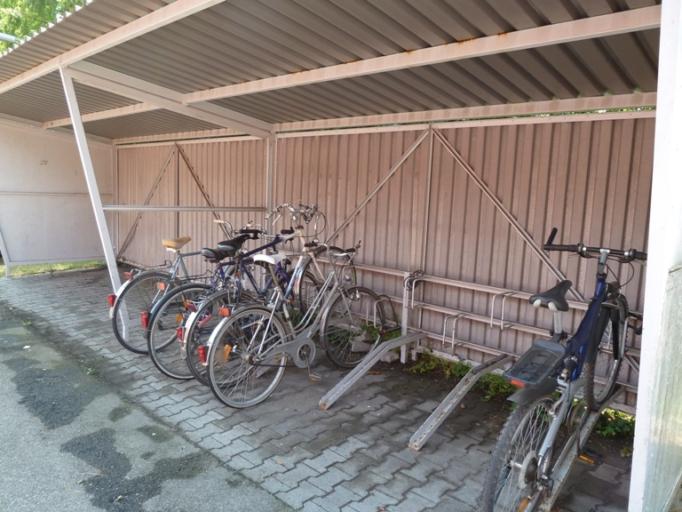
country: DE
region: Baden-Wuerttemberg
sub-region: Tuebingen Region
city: Uberlingen
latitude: 47.7693
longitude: 9.1449
